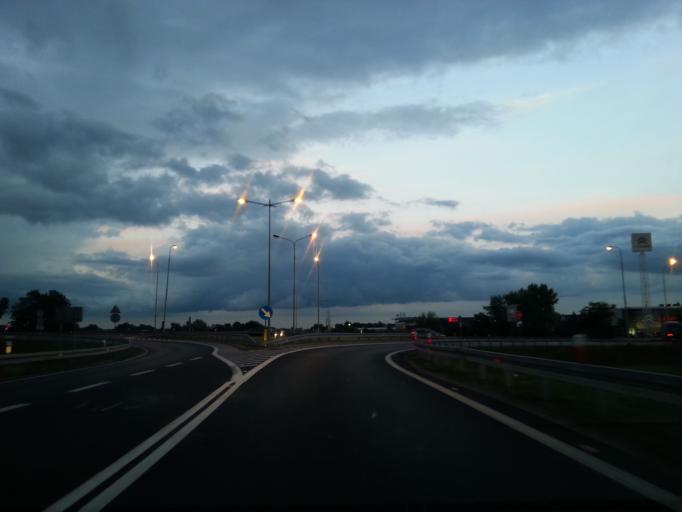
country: PL
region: Lower Silesian Voivodeship
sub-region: Powiat wroclawski
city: Bielany Wroclawskie
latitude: 51.0488
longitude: 16.9705
